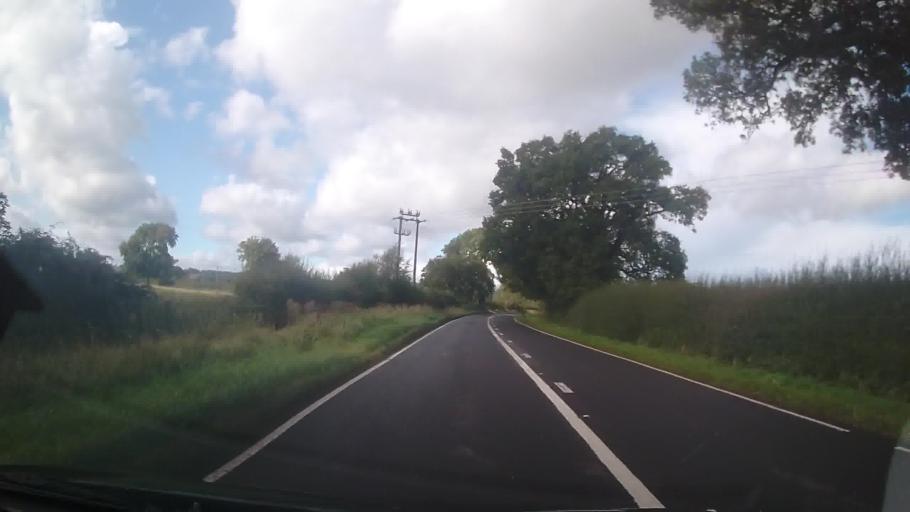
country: GB
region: England
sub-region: Gloucestershire
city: Moreton in Marsh
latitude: 51.9886
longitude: -1.7135
